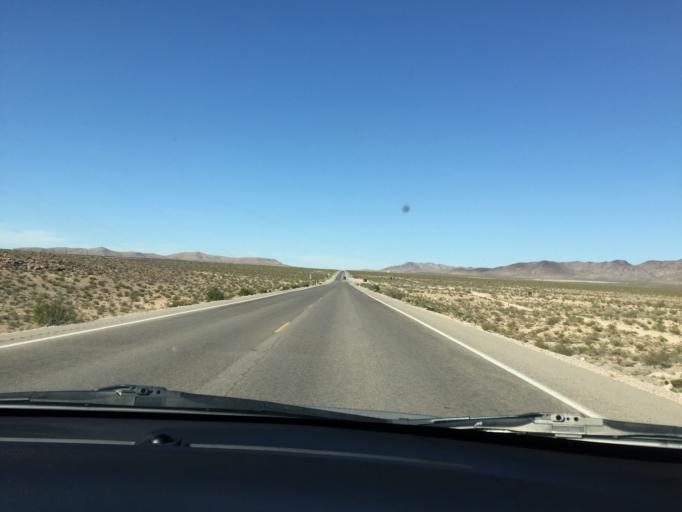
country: US
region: Nevada
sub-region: Clark County
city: Enterprise
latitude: 35.8252
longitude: -115.2863
